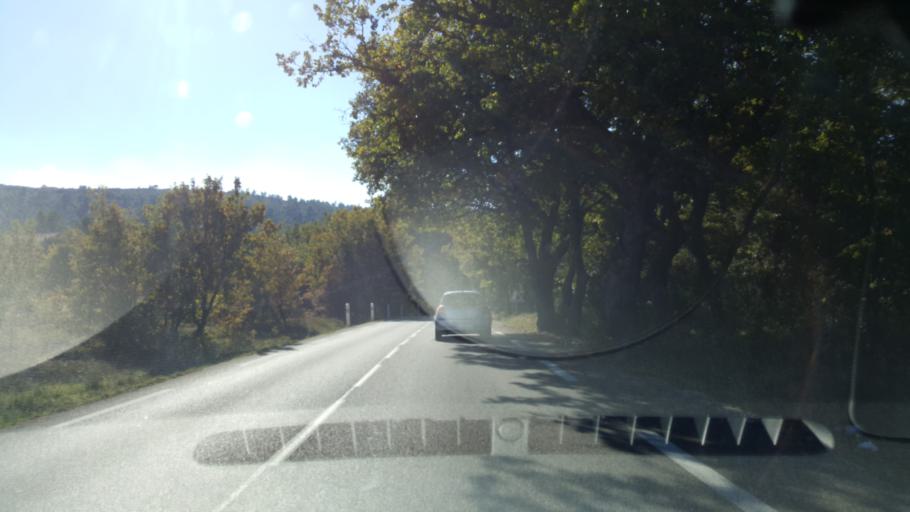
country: FR
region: Provence-Alpes-Cote d'Azur
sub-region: Departement du Var
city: Nans-les-Pins
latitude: 43.3864
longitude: 5.7536
